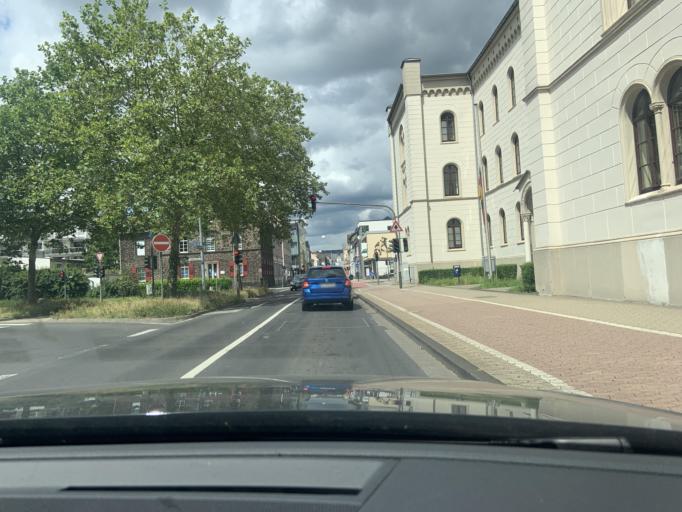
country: DE
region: Rheinland-Pfalz
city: Neuwied
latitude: 50.4277
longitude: 7.4649
